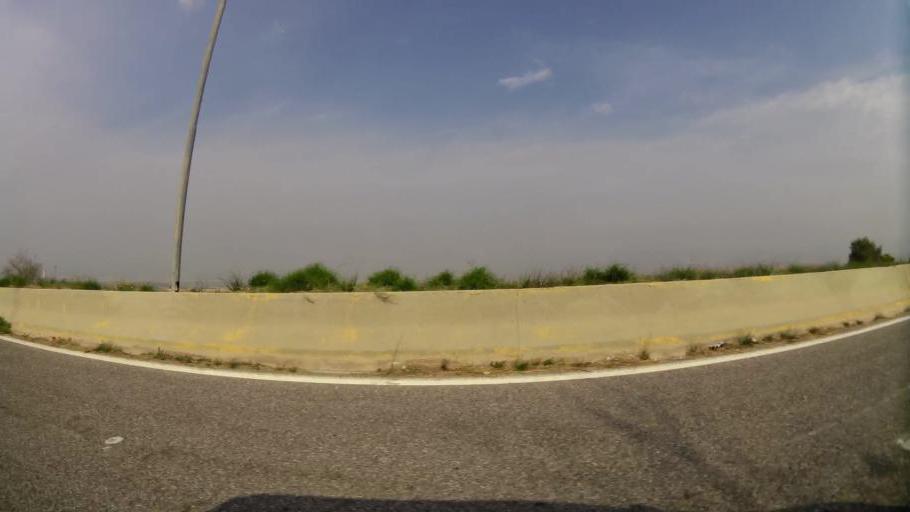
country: GR
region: Attica
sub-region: Nomarchia Athinas
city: Skaramangas
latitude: 38.0291
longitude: 23.6259
